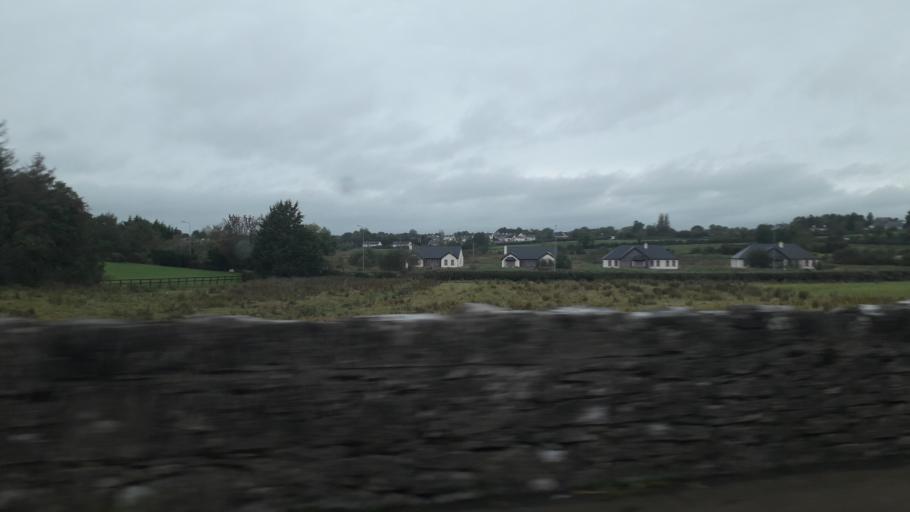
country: IE
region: Leinster
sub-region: An Longfort
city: Lanesborough
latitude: 53.7717
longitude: -8.1031
